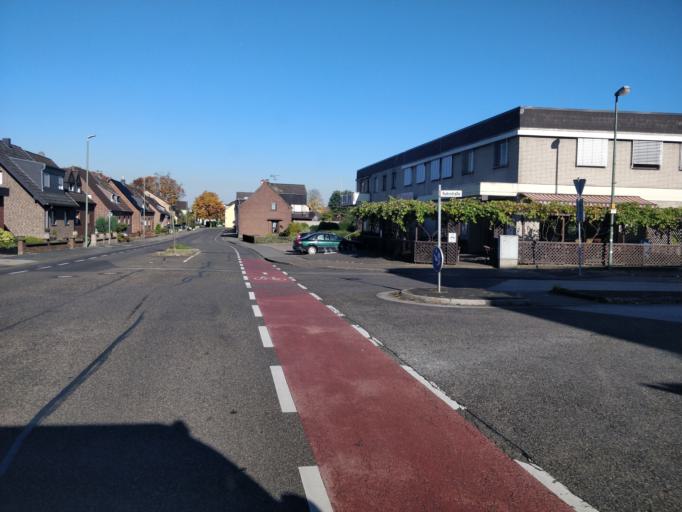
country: DE
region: North Rhine-Westphalia
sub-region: Regierungsbezirk Koln
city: Sinnersdorf
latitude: 51.0621
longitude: 6.8156
